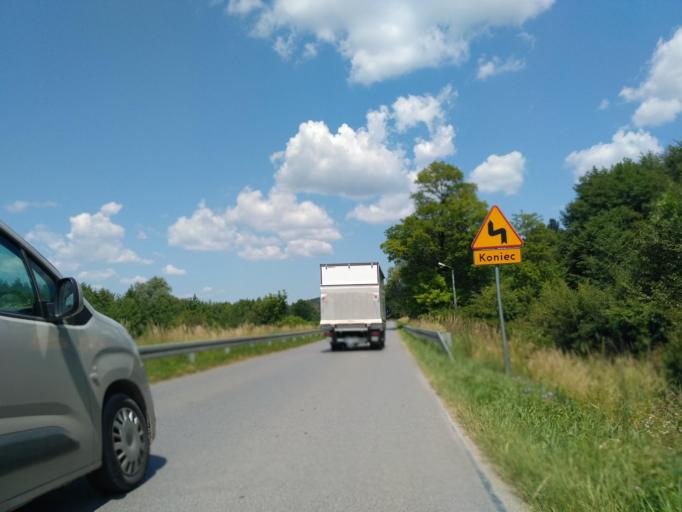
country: PL
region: Subcarpathian Voivodeship
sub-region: Powiat sanocki
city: Niebieszczany
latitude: 49.5349
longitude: 22.1288
